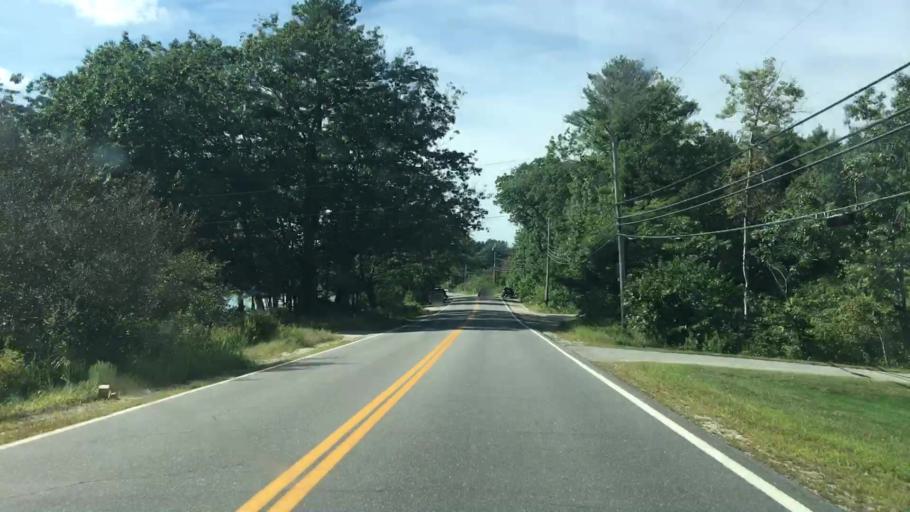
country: US
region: Maine
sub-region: Sagadahoc County
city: Bath
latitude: 43.9301
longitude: -69.8590
